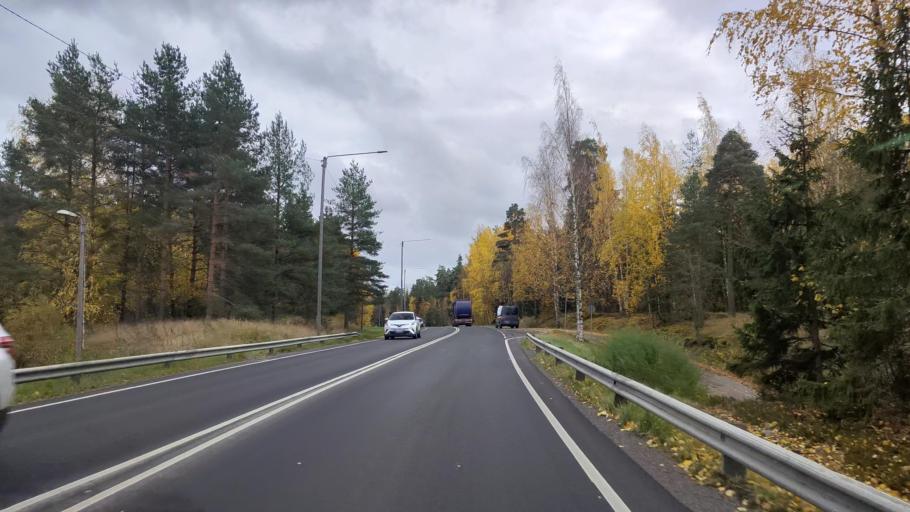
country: FI
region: Varsinais-Suomi
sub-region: Turku
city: Kaarina
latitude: 60.4572
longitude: 22.3660
